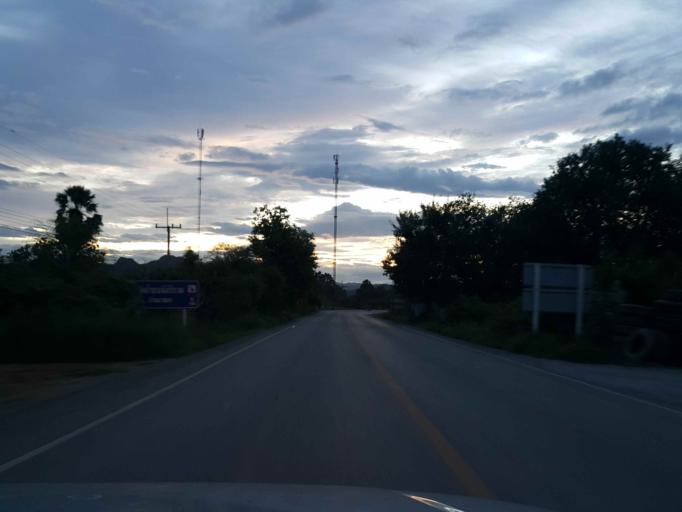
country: TH
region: Sukhothai
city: Thung Saliam
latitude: 17.1766
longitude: 99.6008
